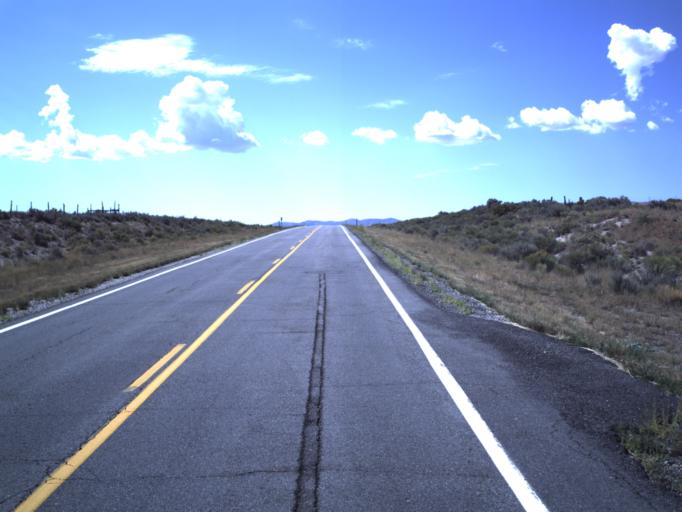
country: US
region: Utah
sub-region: Tooele County
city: Tooele
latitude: 40.1590
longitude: -112.4308
